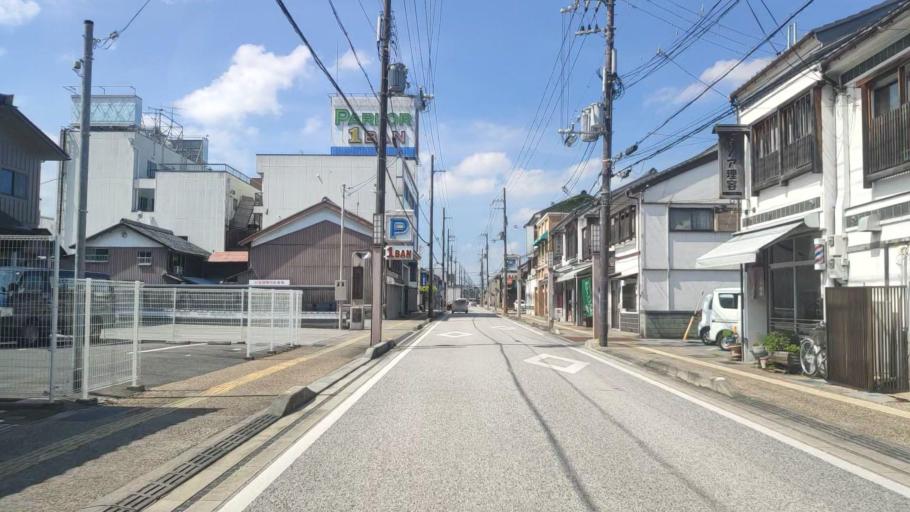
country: JP
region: Shiga Prefecture
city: Hikone
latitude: 35.2716
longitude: 136.2599
